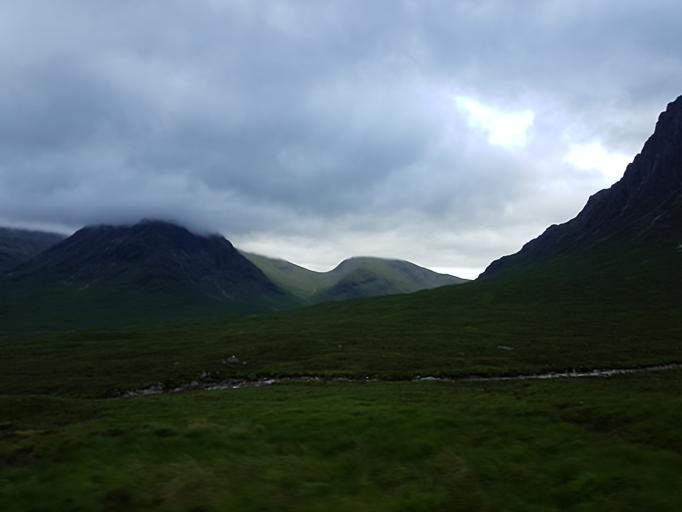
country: GB
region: Scotland
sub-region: Highland
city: Spean Bridge
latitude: 56.6566
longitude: -4.8758
